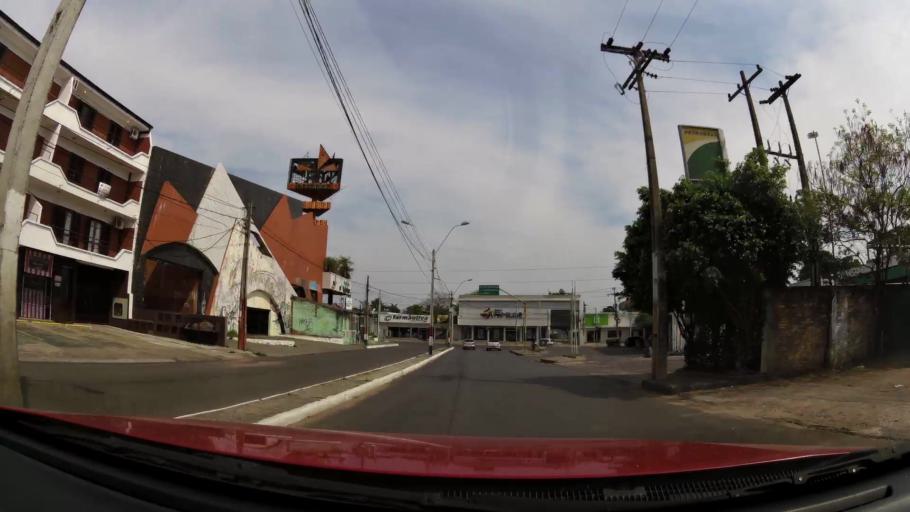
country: PY
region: Asuncion
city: Asuncion
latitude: -25.2566
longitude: -57.5832
